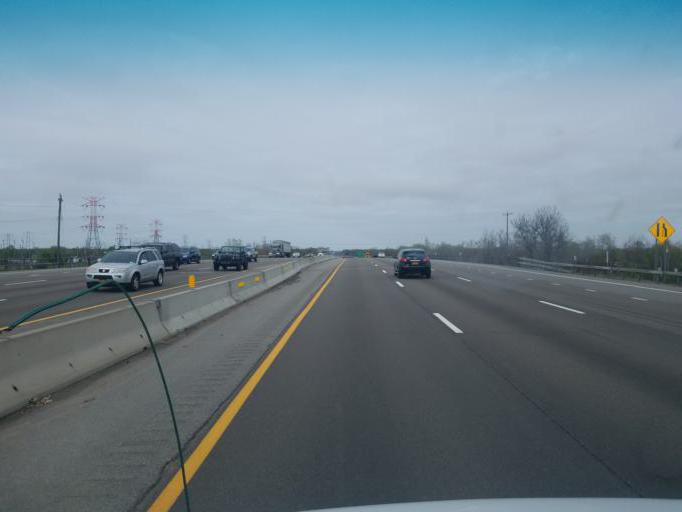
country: US
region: New York
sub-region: Erie County
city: Cheektowaga
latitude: 42.9140
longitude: -78.7664
